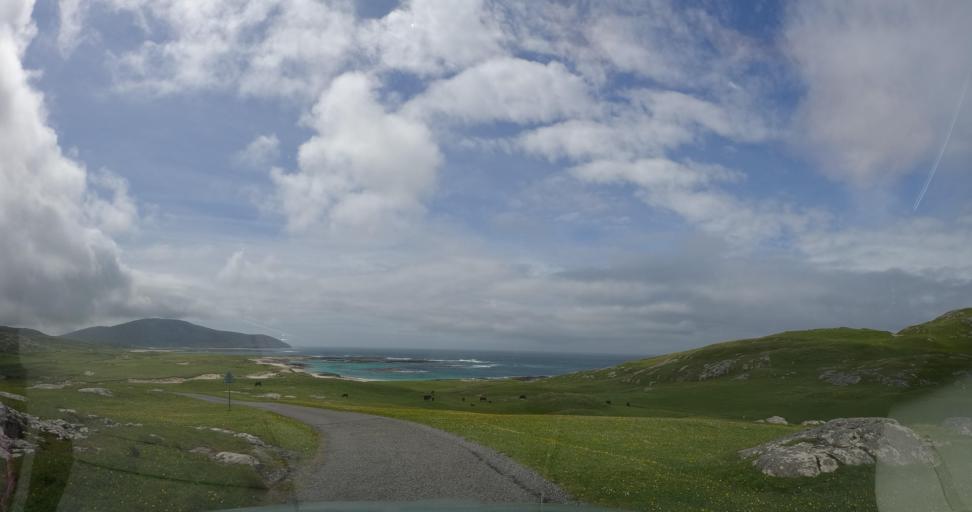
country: GB
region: Scotland
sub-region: Eilean Siar
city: Barra
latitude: 57.0079
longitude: -7.4993
